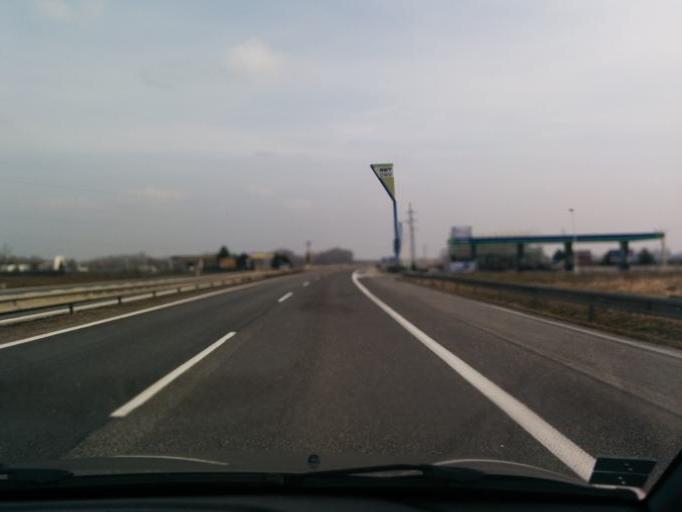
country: SK
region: Trnavsky
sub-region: Okres Galanta
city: Galanta
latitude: 48.2589
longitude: 17.7533
